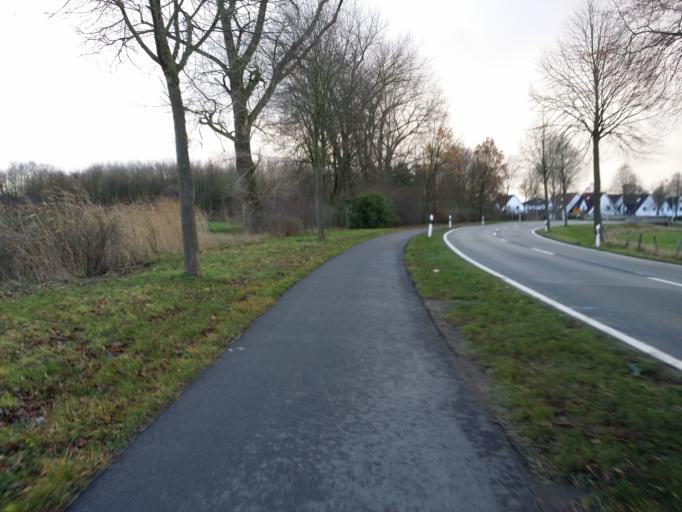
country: DE
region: Lower Saxony
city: Riede
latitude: 52.9895
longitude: 8.8945
